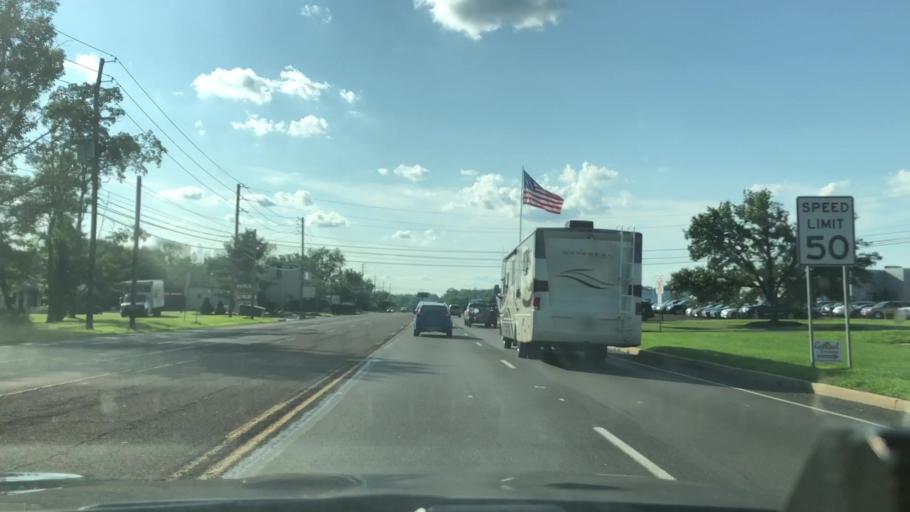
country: US
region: Pennsylvania
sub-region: Montgomery County
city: Hatfield
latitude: 40.2999
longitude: -75.2865
